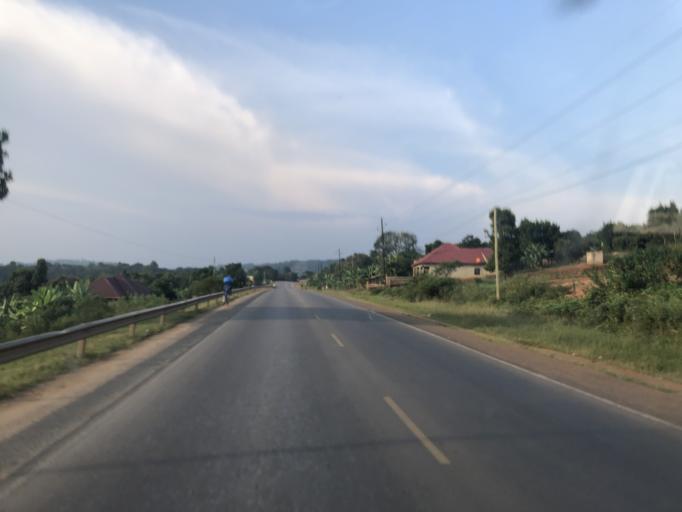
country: UG
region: Central Region
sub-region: Mpigi District
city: Mpigi
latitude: 0.1974
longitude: 32.2983
